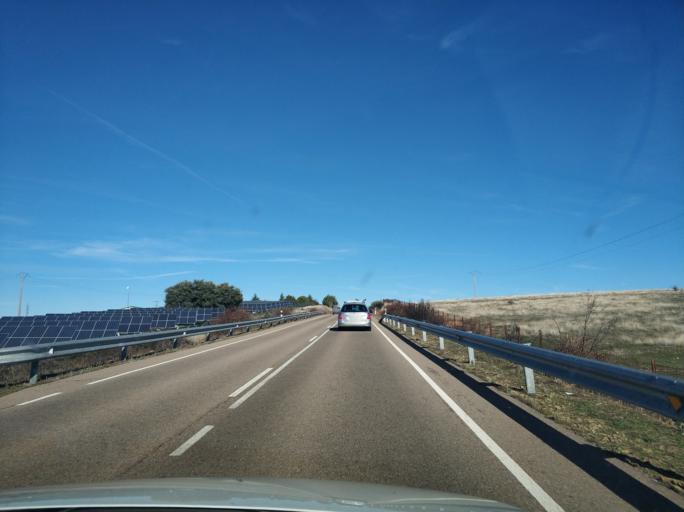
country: ES
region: Castille and Leon
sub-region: Provincia de Salamanca
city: Herguijuela del Campo
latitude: 40.6620
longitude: -5.8980
